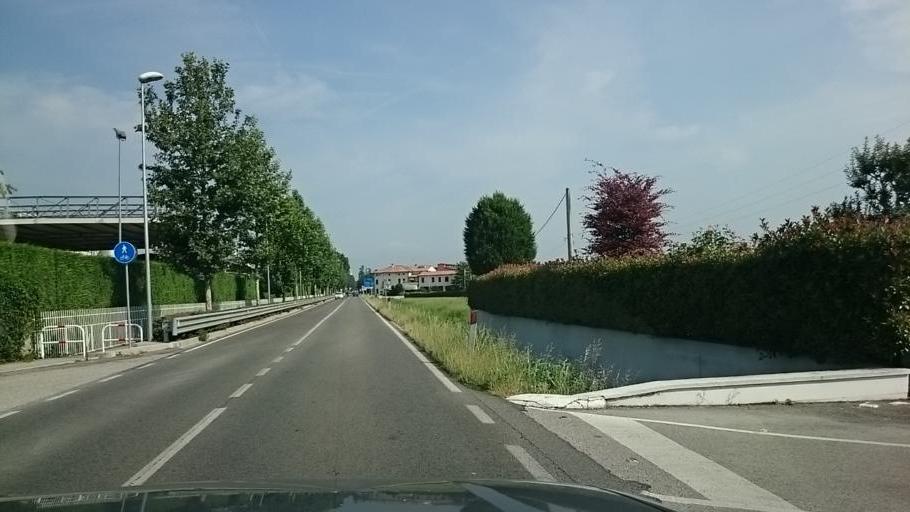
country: IT
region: Veneto
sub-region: Provincia di Treviso
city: Castelfranco Veneto
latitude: 45.6529
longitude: 11.9425
